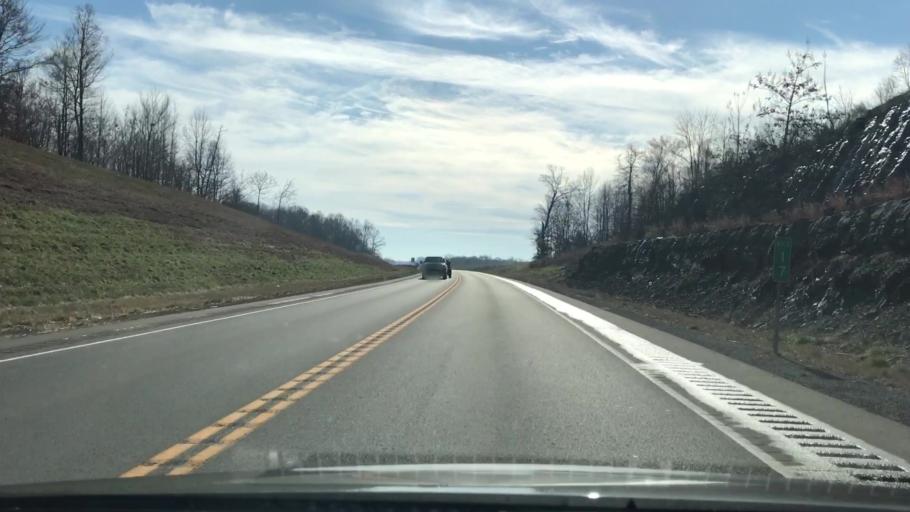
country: US
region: Kentucky
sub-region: Monroe County
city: Tompkinsville
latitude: 36.8218
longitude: -85.6885
